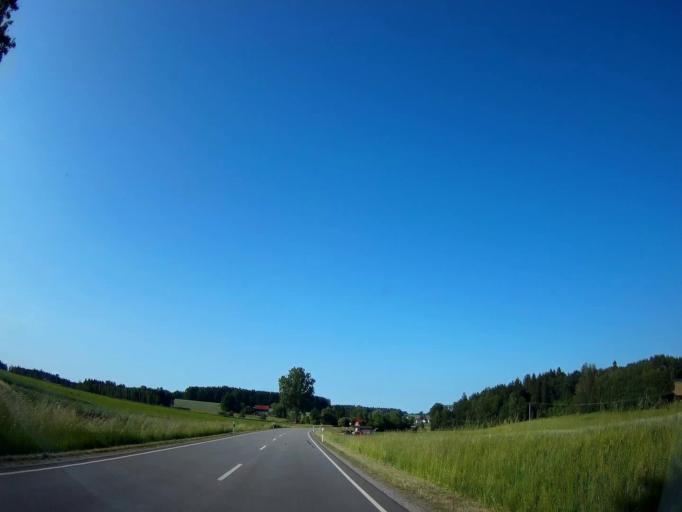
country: DE
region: Bavaria
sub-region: Lower Bavaria
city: Falkenberg
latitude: 48.4749
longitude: 12.7328
